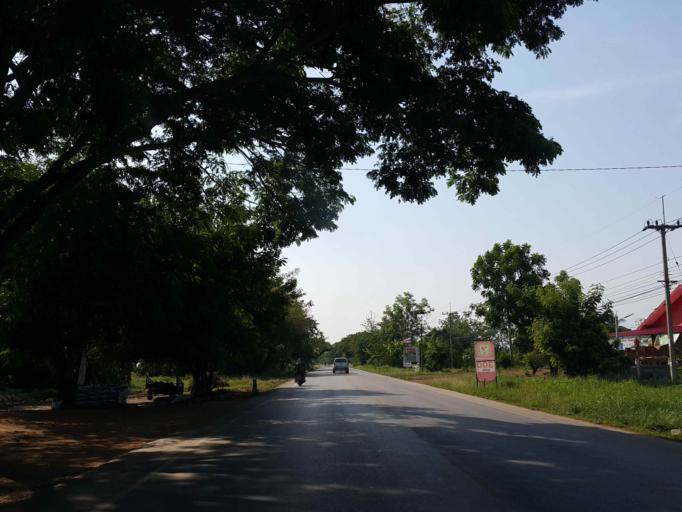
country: TH
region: Sukhothai
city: Thung Saliam
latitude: 17.3310
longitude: 99.6213
